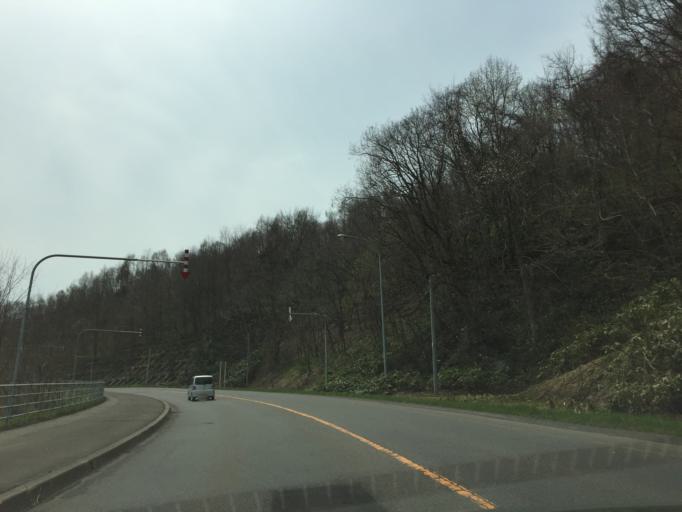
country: JP
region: Hokkaido
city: Ashibetsu
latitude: 43.5622
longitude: 142.1804
